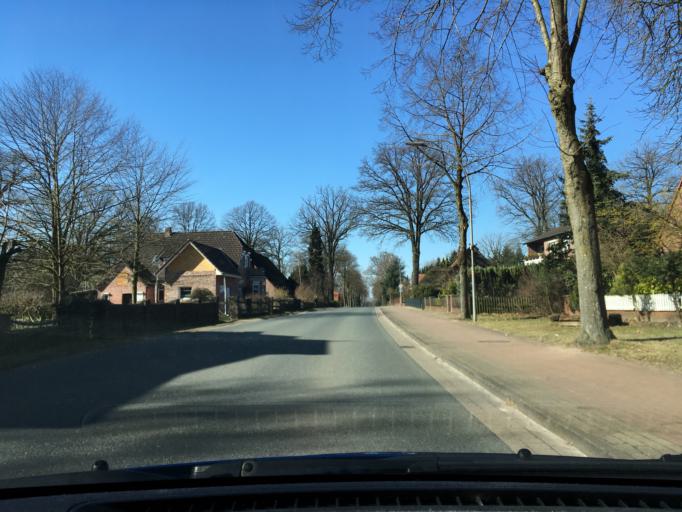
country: DE
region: Lower Saxony
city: Neuenkirchen
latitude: 53.0664
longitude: 9.6617
